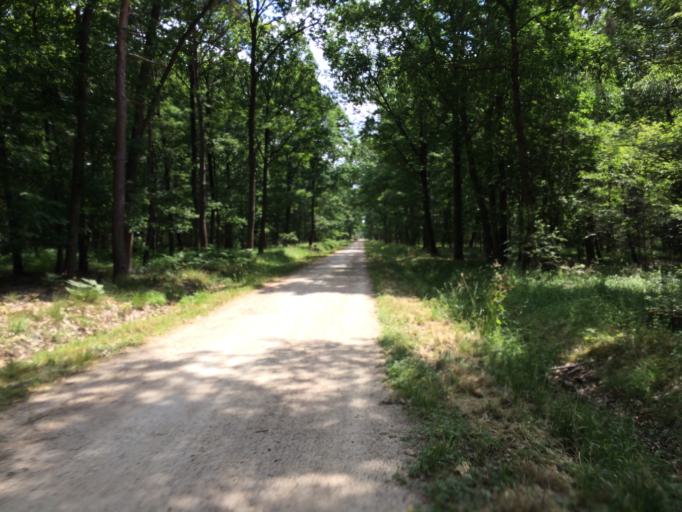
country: FR
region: Ile-de-France
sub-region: Departement de l'Essonne
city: Epinay-sous-Senart
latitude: 48.6689
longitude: 2.4992
